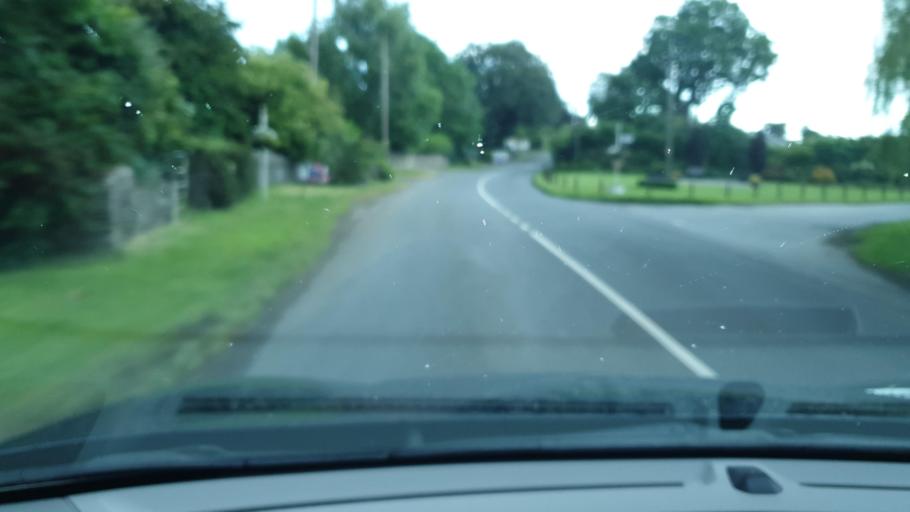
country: IE
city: Kentstown
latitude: 53.6043
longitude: -6.6077
